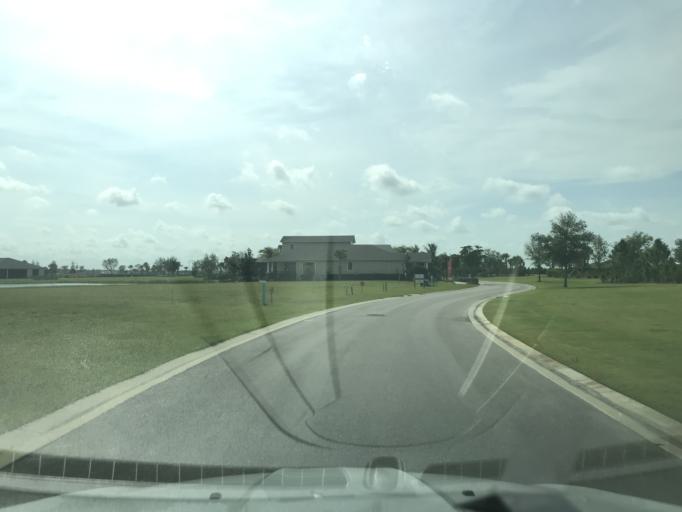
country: US
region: Florida
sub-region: Lee County
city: Fort Myers Shores
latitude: 26.7833
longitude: -81.7524
